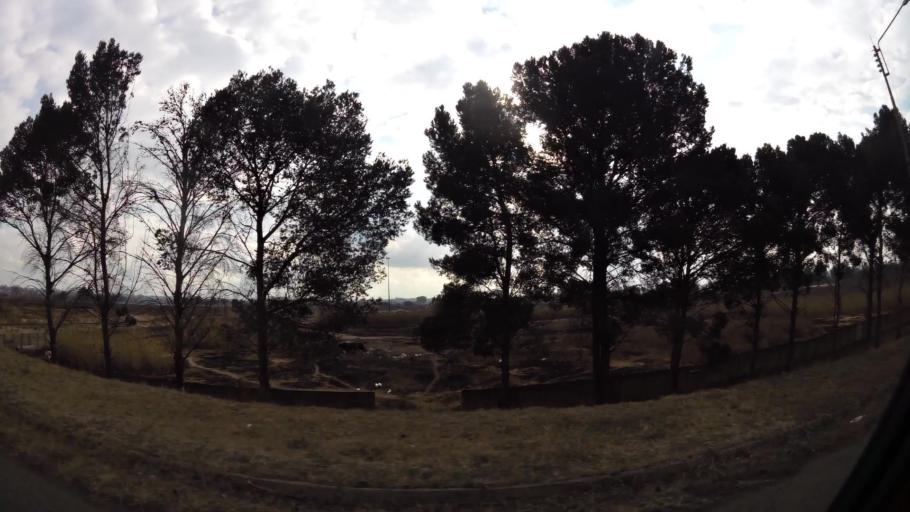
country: ZA
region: Gauteng
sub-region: Sedibeng District Municipality
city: Vereeniging
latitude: -26.6746
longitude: 27.8980
